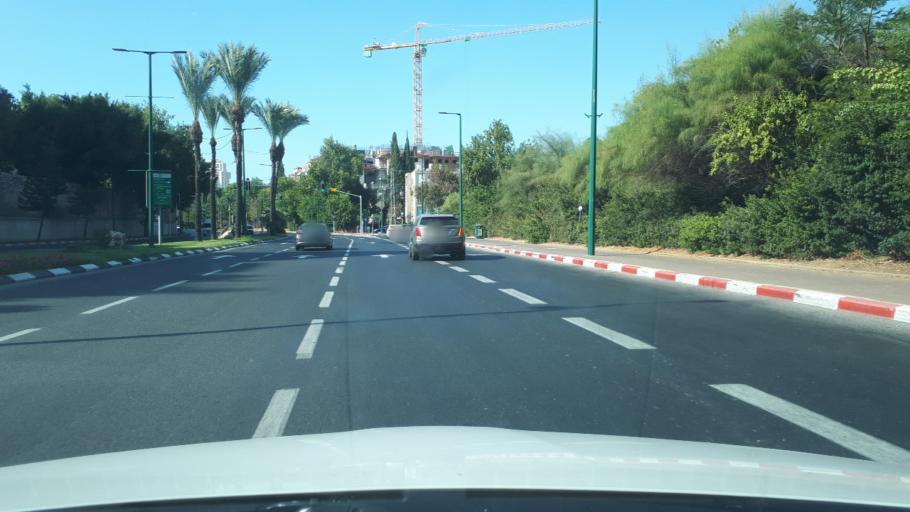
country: IL
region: Tel Aviv
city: Giv`atayim
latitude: 32.0604
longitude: 34.8210
